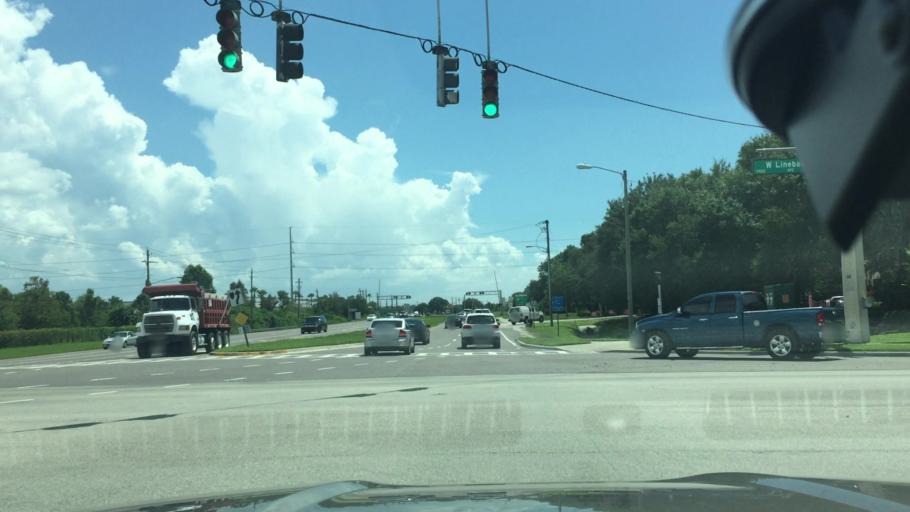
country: US
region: Florida
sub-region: Hillsborough County
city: Carrollwood Village
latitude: 28.0402
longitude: -82.5420
